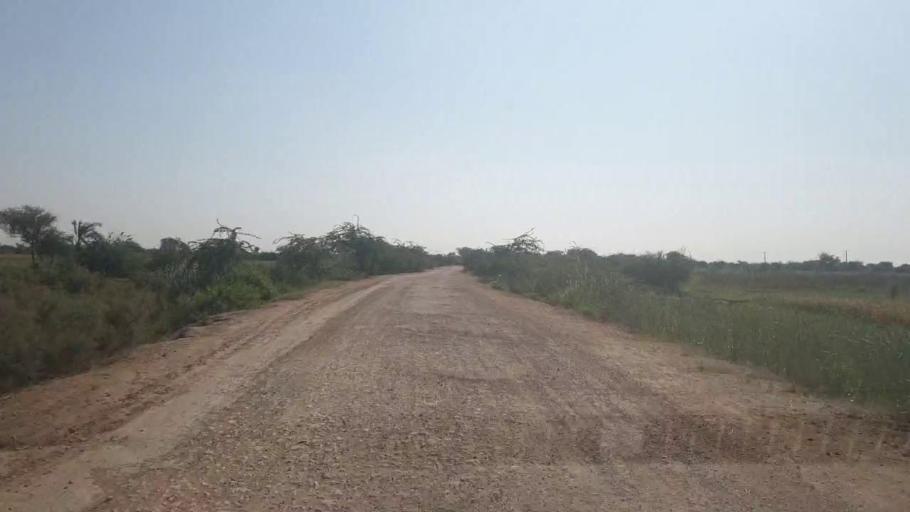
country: PK
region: Sindh
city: Badin
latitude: 24.5873
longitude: 68.8458
